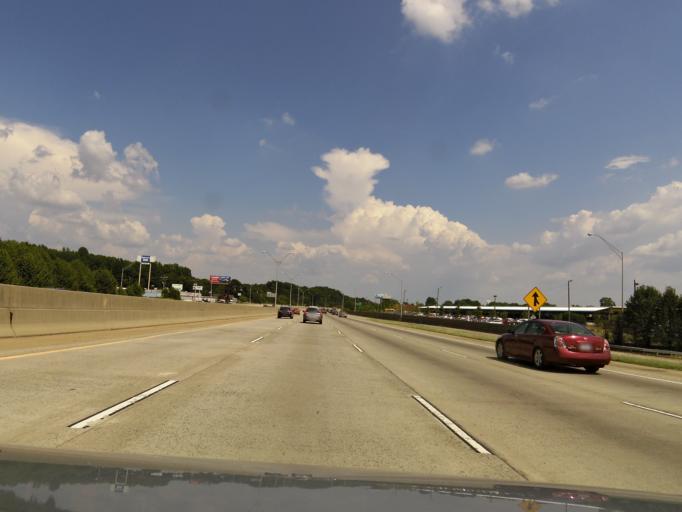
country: US
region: North Carolina
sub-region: Mecklenburg County
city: Charlotte
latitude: 35.2412
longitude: -80.9378
